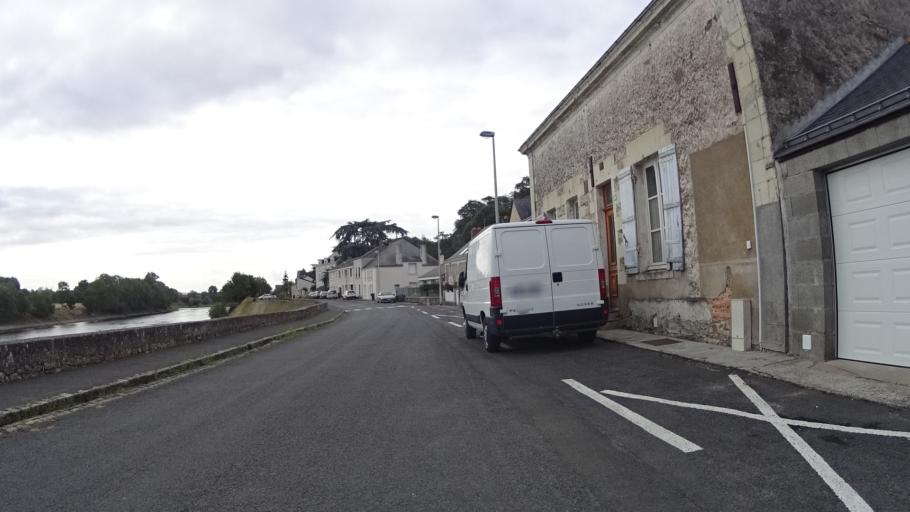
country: FR
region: Pays de la Loire
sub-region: Departement de Maine-et-Loire
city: Montjean-sur-Loire
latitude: 47.3900
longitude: -0.8587
